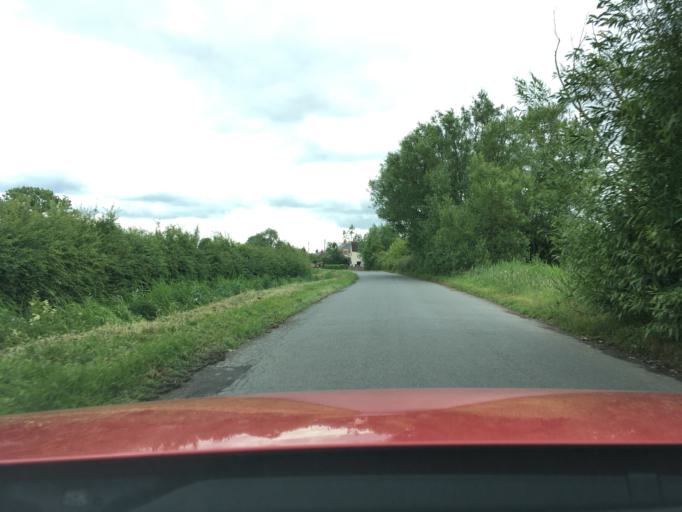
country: GB
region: England
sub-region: Gloucestershire
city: Stonehouse
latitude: 51.7866
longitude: -2.3645
